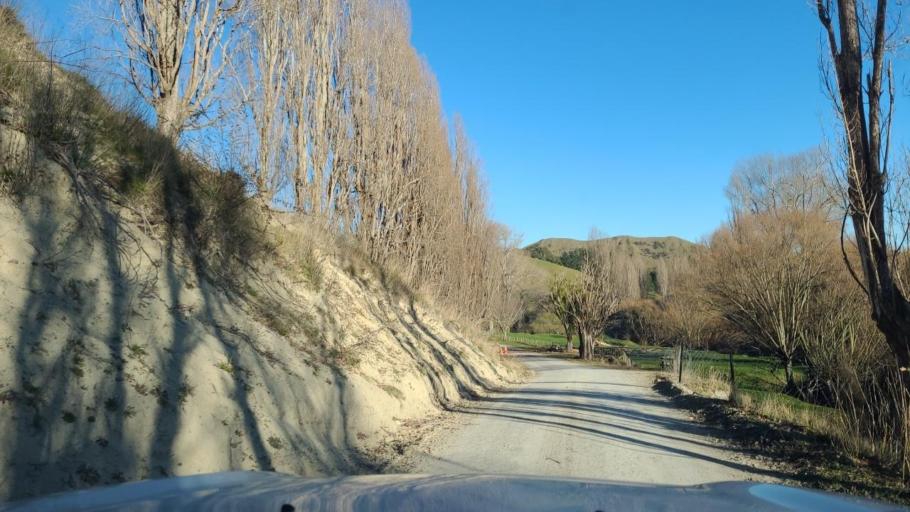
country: NZ
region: Hawke's Bay
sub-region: Hastings District
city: Hastings
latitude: -39.8011
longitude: 176.8386
